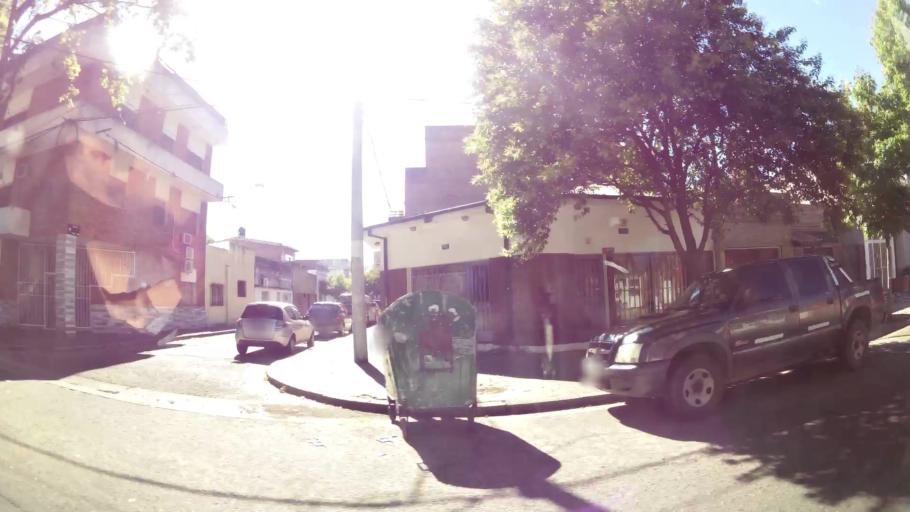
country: AR
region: Santa Fe
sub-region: Departamento de Rosario
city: Rosario
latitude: -32.9473
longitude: -60.6798
